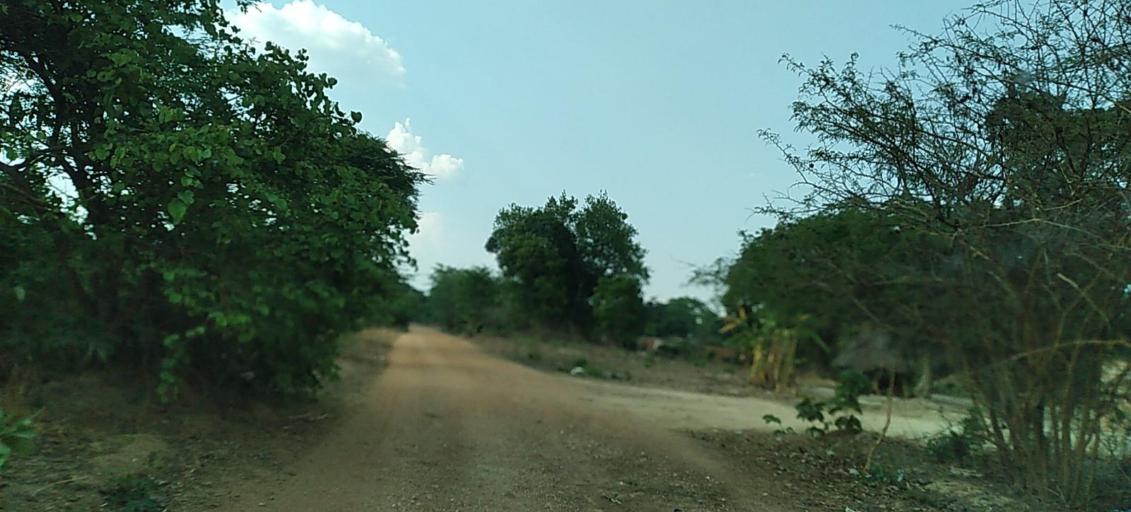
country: ZM
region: Copperbelt
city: Mpongwe
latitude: -13.4871
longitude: 28.0842
